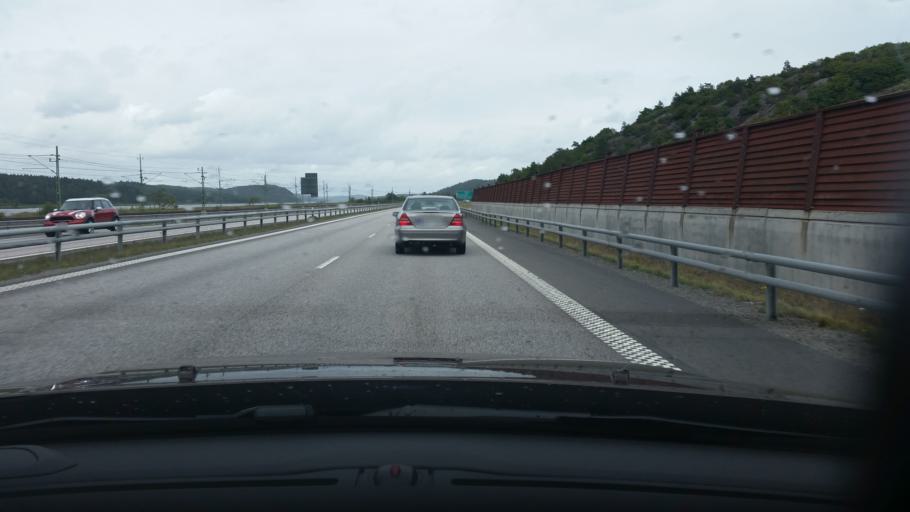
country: SE
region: Vaestra Goetaland
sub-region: Ale Kommun
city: Surte
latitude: 57.8636
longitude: 12.0201
